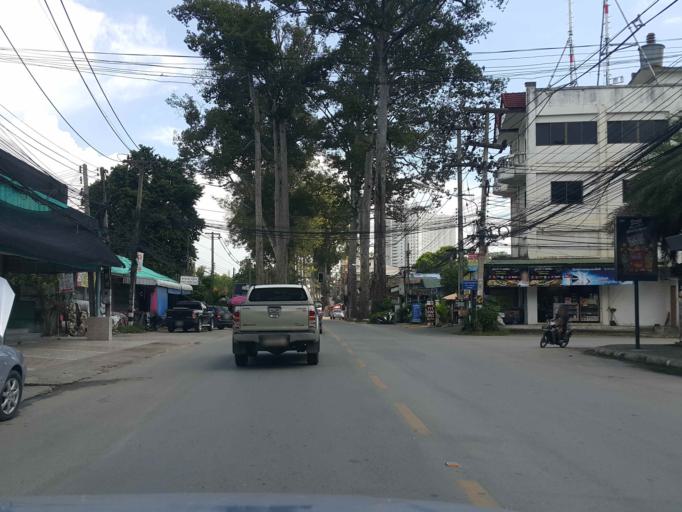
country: TH
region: Chiang Mai
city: Chiang Mai
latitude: 18.7720
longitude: 99.0066
